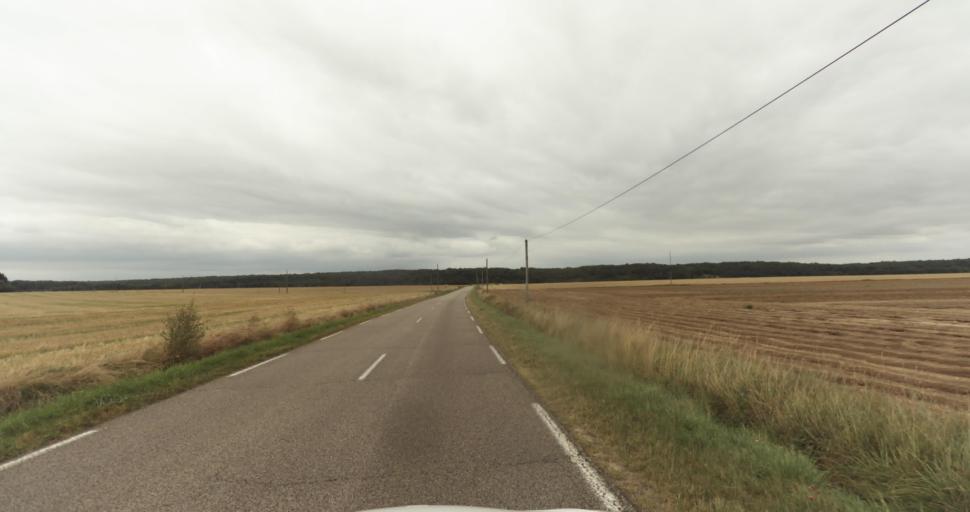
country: FR
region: Haute-Normandie
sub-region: Departement de l'Eure
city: Arnieres-sur-Iton
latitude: 48.9609
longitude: 1.0692
